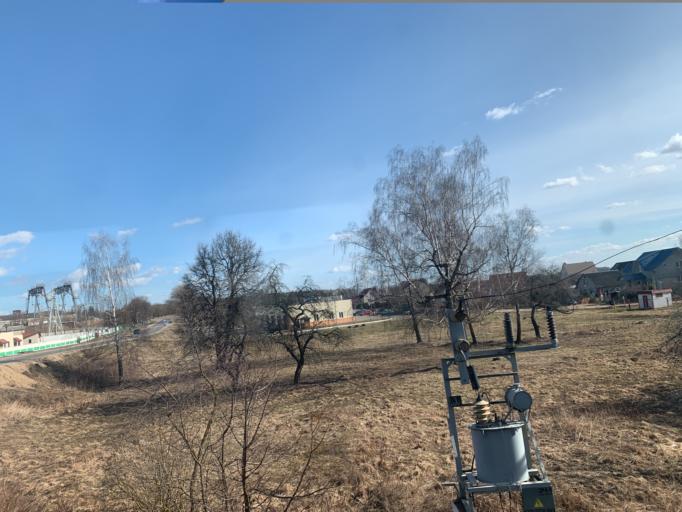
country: BY
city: Fanipol
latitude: 53.7371
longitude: 27.3203
